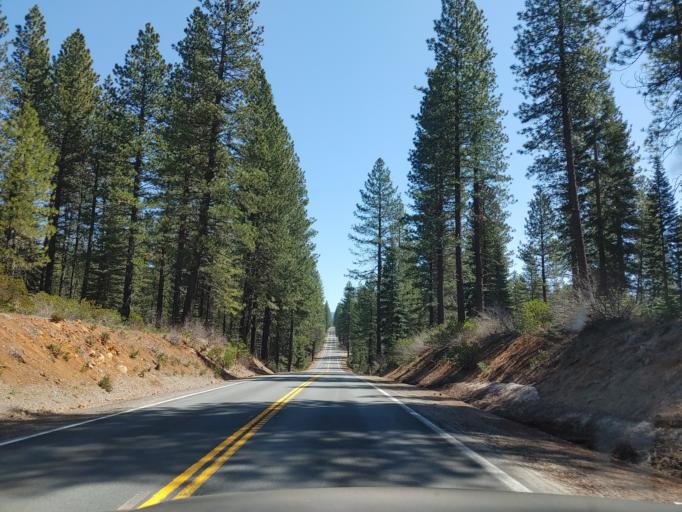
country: US
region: California
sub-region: Siskiyou County
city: McCloud
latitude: 41.2665
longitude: -121.8831
